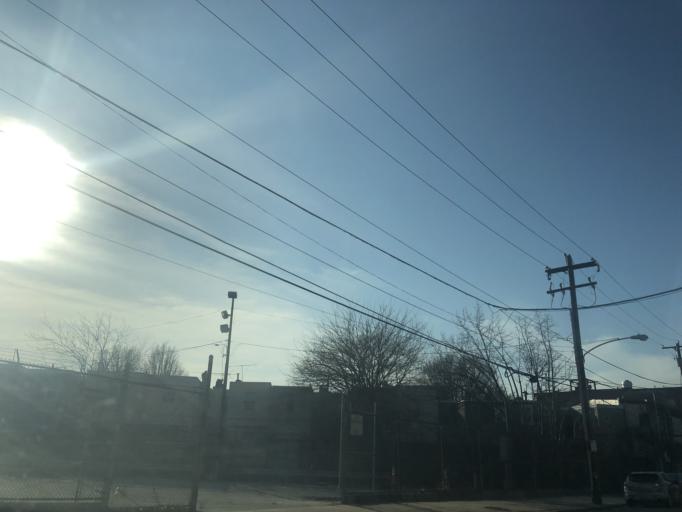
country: US
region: Pennsylvania
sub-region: Philadelphia County
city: Philadelphia
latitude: 39.9324
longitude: -75.1632
